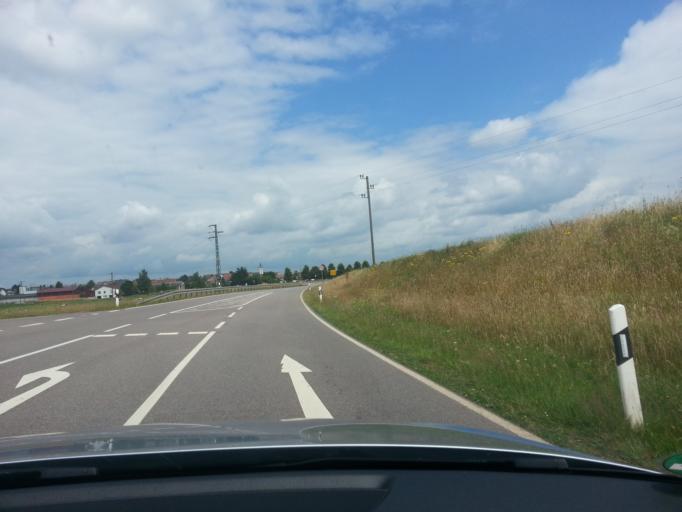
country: DE
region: Saarland
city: Orscholz
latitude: 49.4976
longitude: 6.5171
